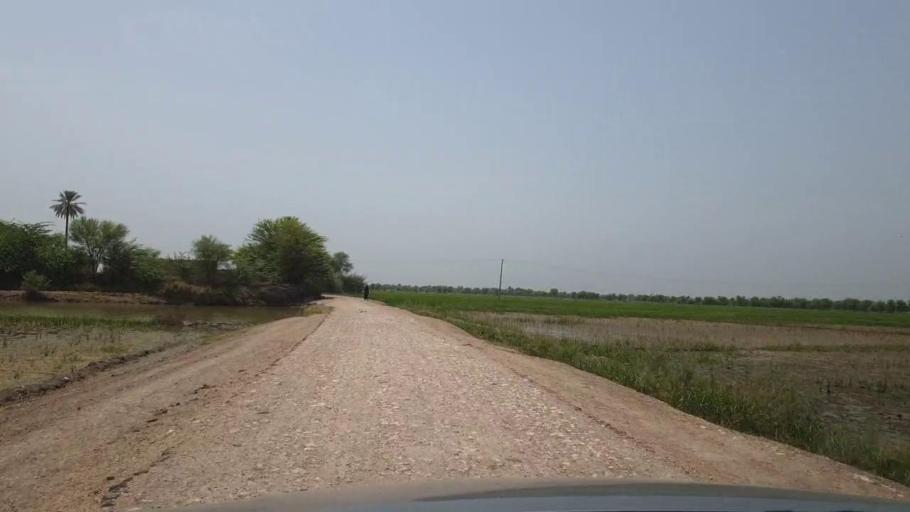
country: PK
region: Sindh
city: Madeji
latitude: 27.7754
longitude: 68.4058
